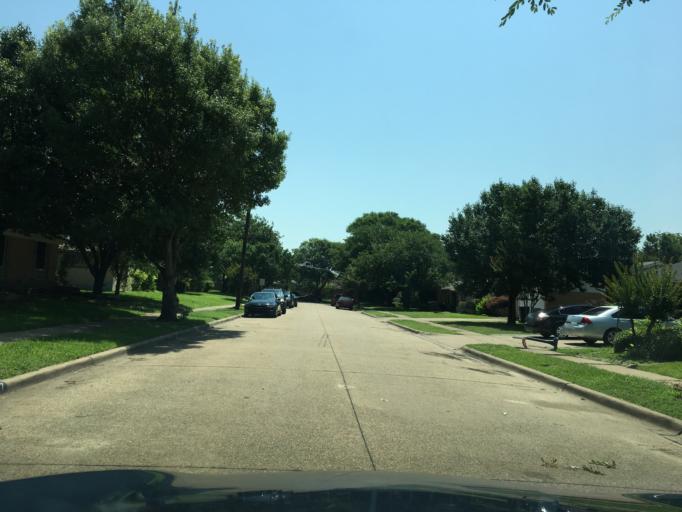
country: US
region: Texas
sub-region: Dallas County
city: Garland
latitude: 32.9218
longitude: -96.6849
